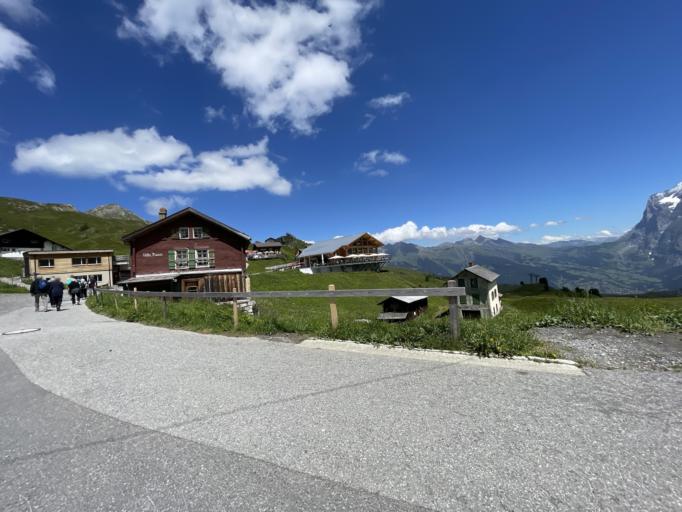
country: CH
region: Bern
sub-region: Interlaken-Oberhasli District
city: Lauterbrunnen
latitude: 46.5855
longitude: 7.9610
